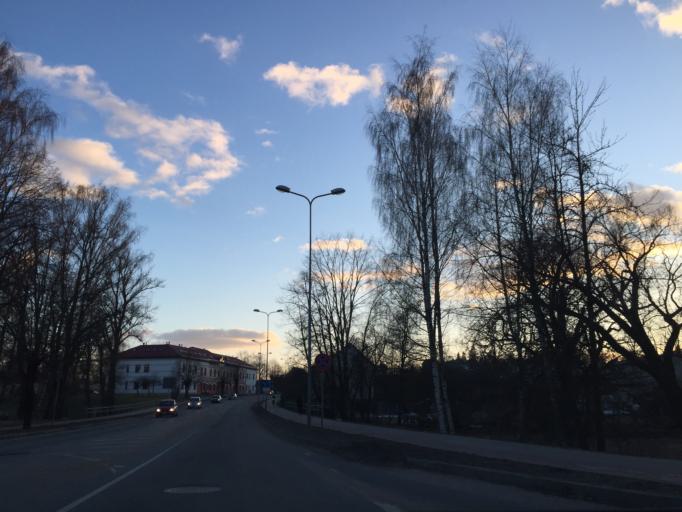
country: LV
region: Valmieras Rajons
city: Valmiera
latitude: 57.5359
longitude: 25.4051
